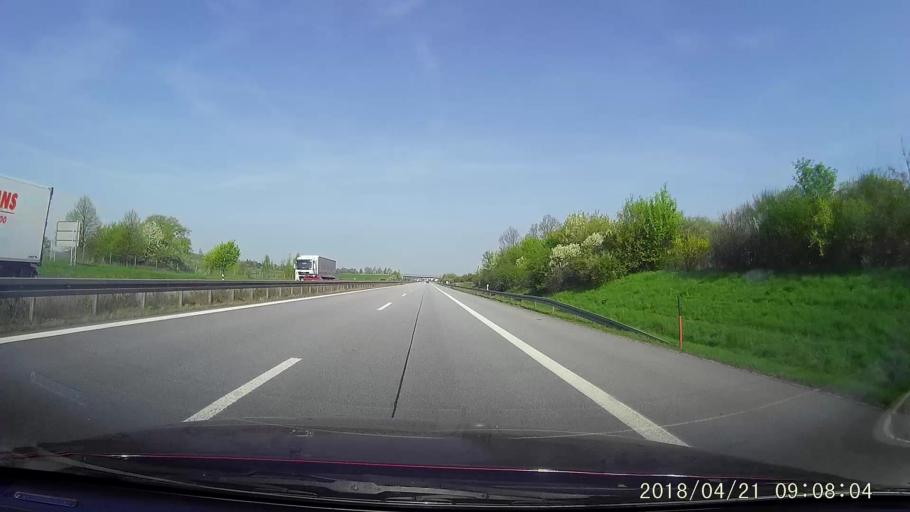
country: DE
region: Saxony
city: Kodersdorf
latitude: 51.2073
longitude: 14.9455
